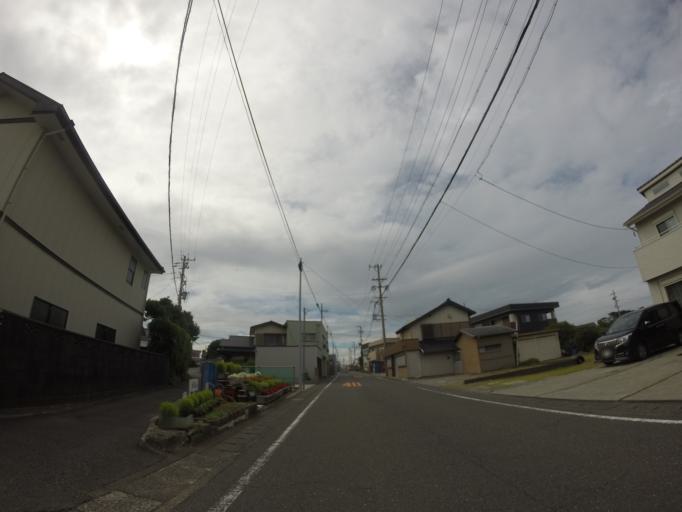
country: JP
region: Shizuoka
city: Oyama
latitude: 34.6057
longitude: 138.2135
